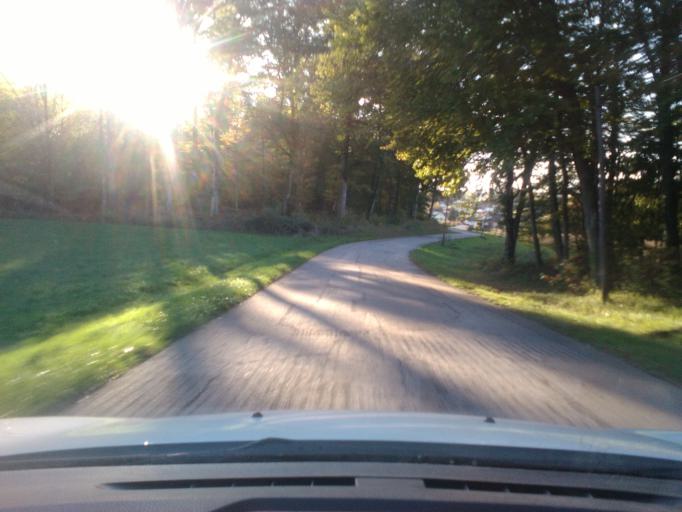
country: FR
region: Lorraine
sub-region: Departement des Vosges
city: Chatel-sur-Moselle
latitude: 48.3173
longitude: 6.4146
